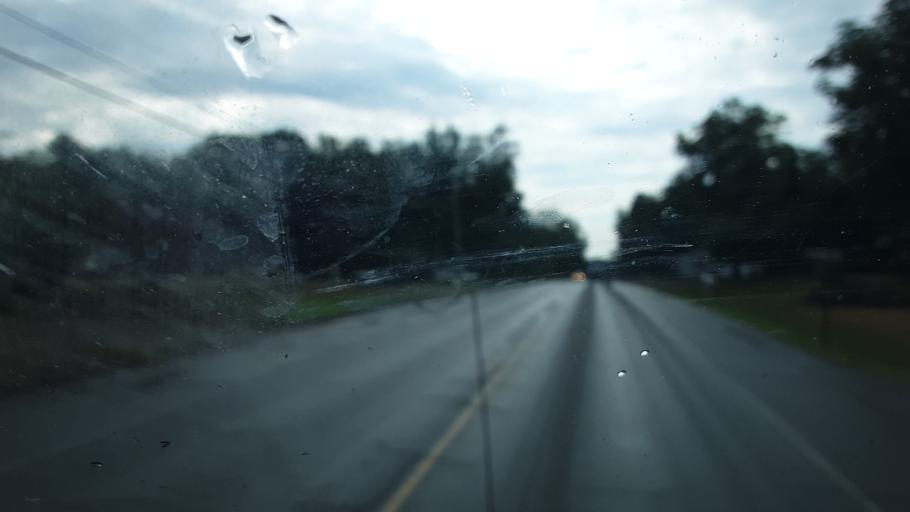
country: US
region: Maine
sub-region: Penobscot County
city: Milford
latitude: 44.9504
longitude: -68.6953
